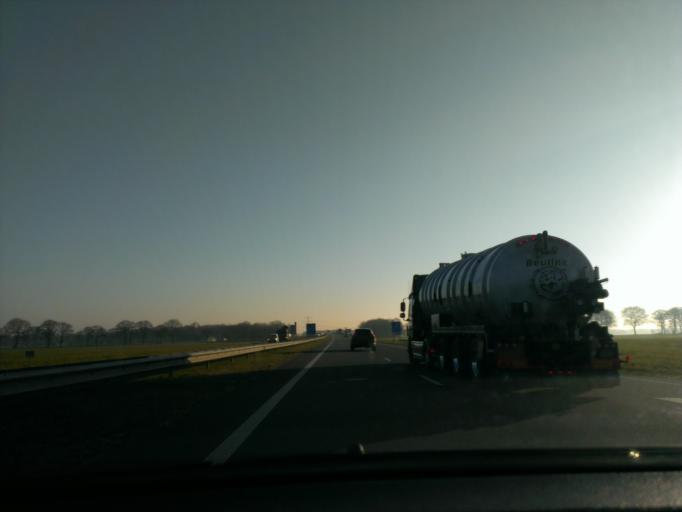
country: NL
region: Drenthe
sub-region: Gemeente Coevorden
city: Sleen
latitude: 52.7521
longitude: 6.8290
